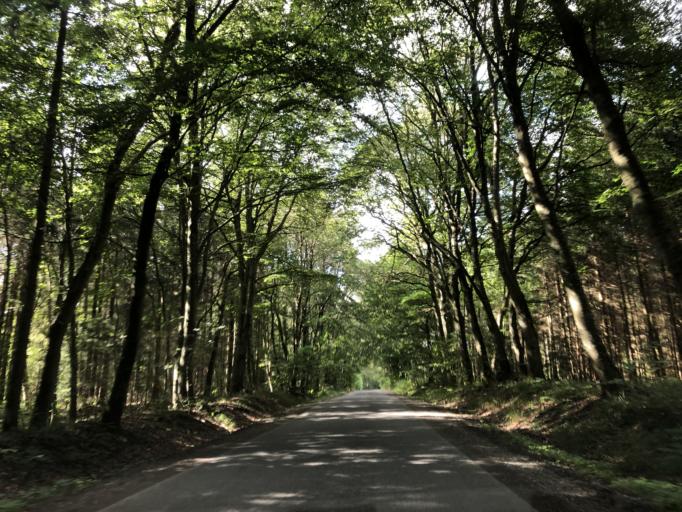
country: DK
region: Central Jutland
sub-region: Skanderborg Kommune
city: Galten
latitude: 56.1747
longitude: 9.9234
